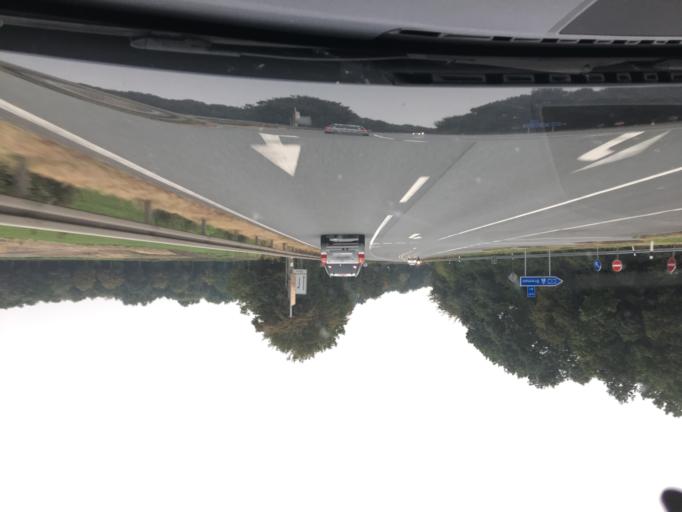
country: DE
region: North Rhine-Westphalia
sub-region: Regierungsbezirk Munster
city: Greven
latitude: 52.0835
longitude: 7.6445
